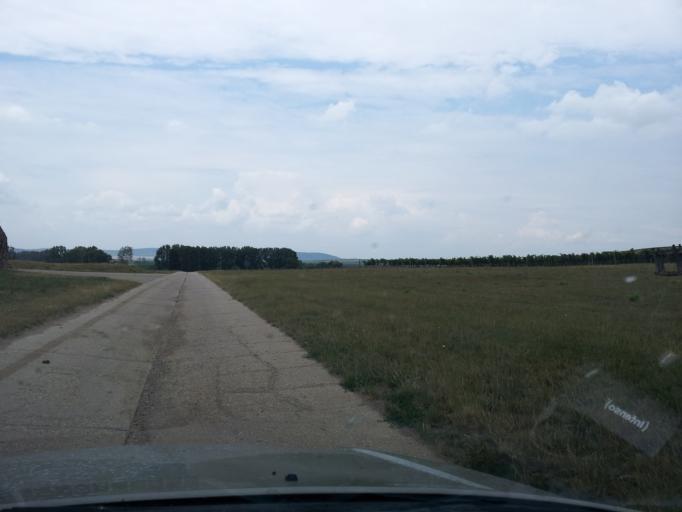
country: HU
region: Borsod-Abauj-Zemplen
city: Mad
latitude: 48.1667
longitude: 21.2988
